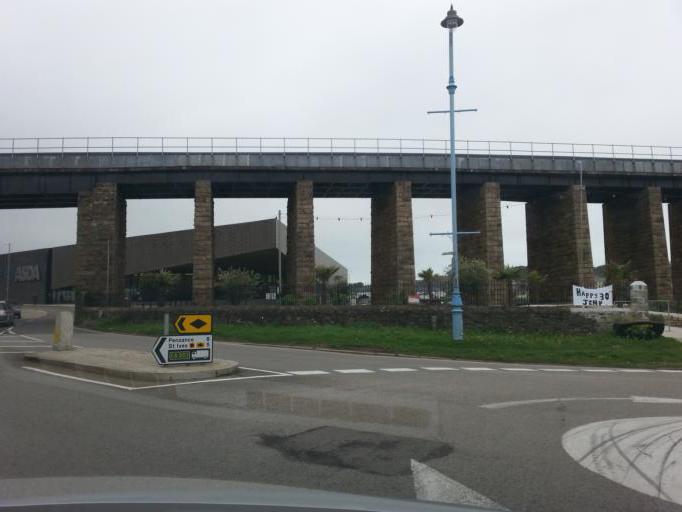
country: GB
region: England
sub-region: Cornwall
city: Hayle
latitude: 50.1841
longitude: -5.4214
